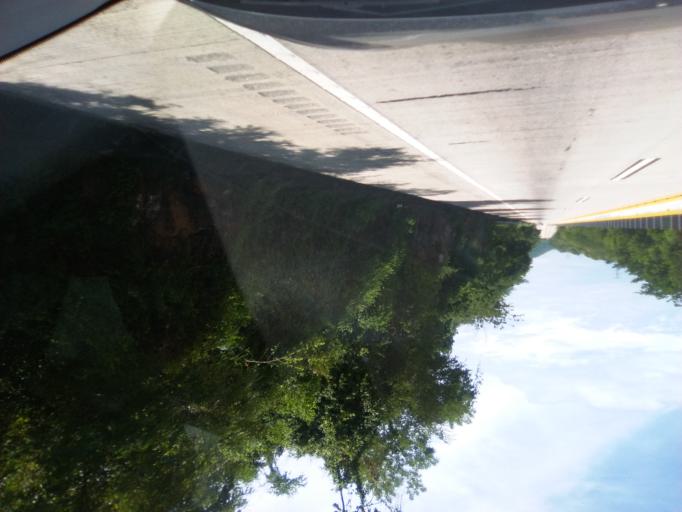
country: MX
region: Guerrero
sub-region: Acapulco de Juarez
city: Kilometro 30
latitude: 17.0011
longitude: -99.6833
